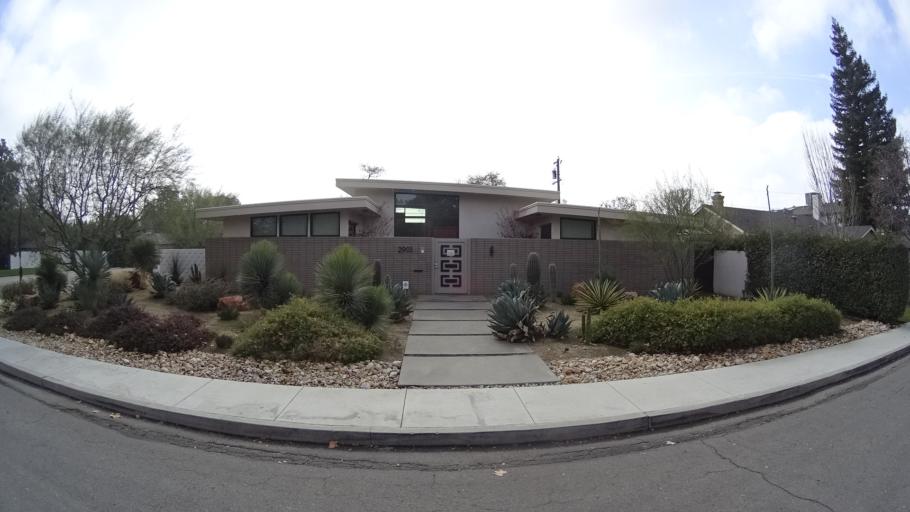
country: US
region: California
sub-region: Kern County
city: Bakersfield
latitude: 35.3772
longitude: -119.0355
